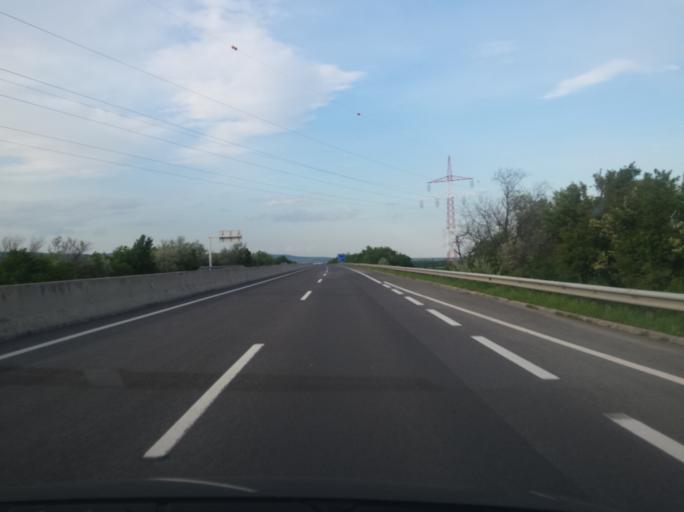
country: AT
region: Burgenland
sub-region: Politischer Bezirk Mattersburg
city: Hirm
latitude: 47.8043
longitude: 16.4750
